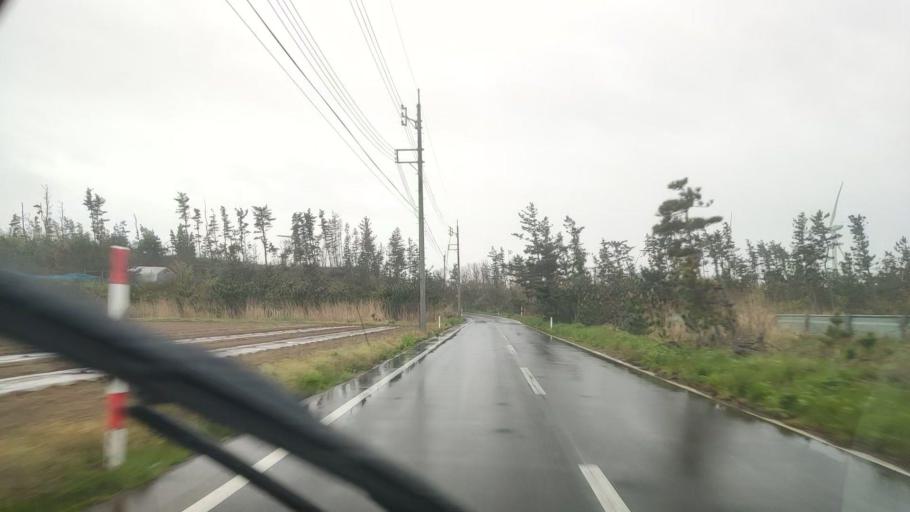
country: JP
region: Akita
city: Noshiromachi
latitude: 40.0813
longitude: 139.9550
